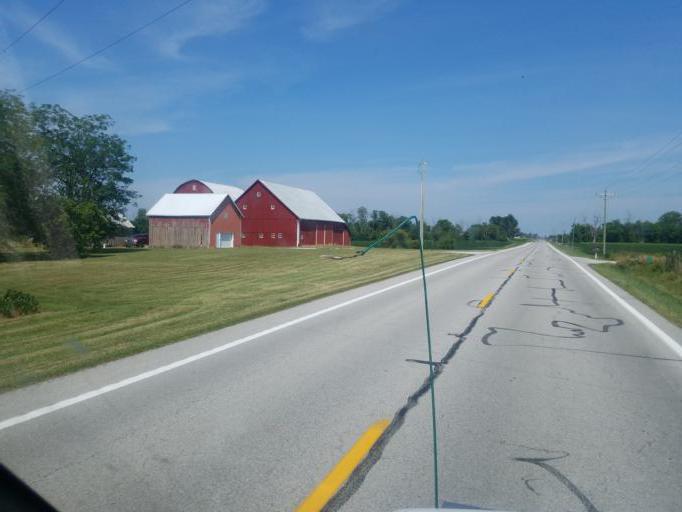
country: US
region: Ohio
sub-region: Auglaize County
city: Saint Marys
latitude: 40.4952
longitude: -84.3732
